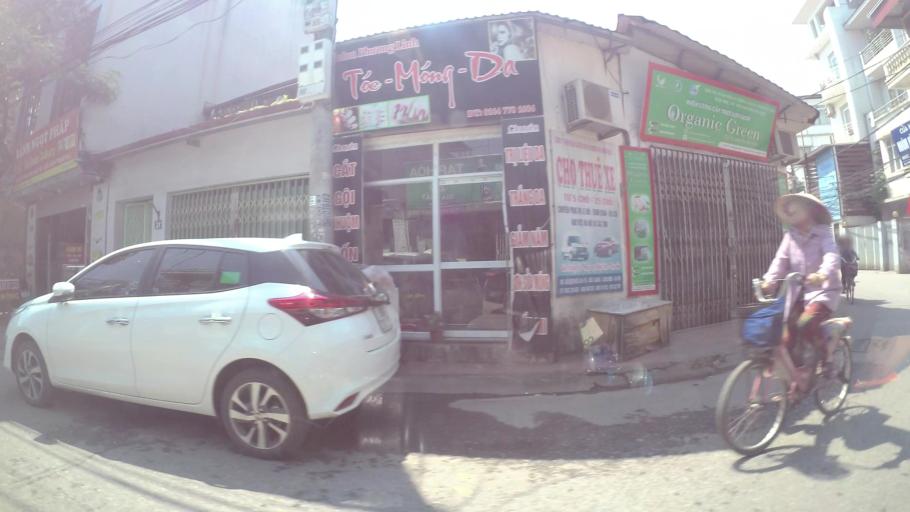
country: VN
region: Ha Noi
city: Hoan Kiem
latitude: 21.0522
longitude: 105.8778
